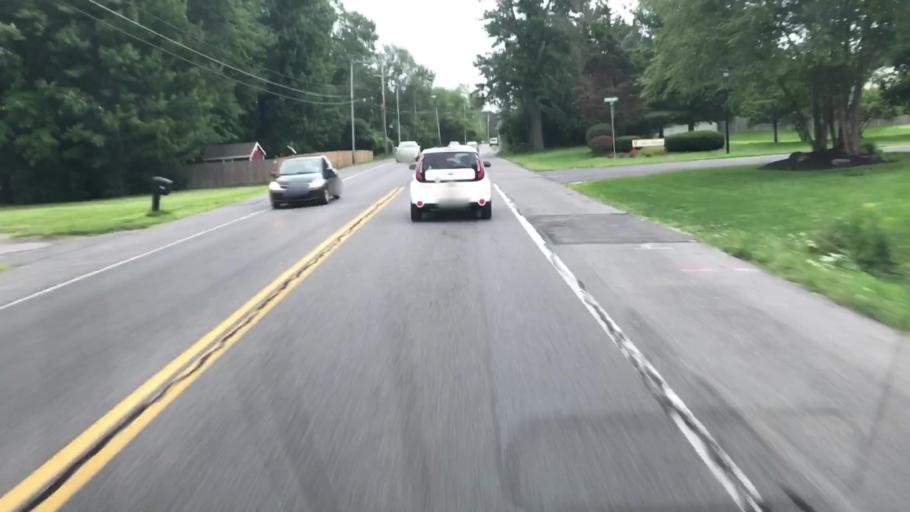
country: US
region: New York
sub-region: Onondaga County
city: North Syracuse
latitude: 43.1352
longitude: -76.1686
